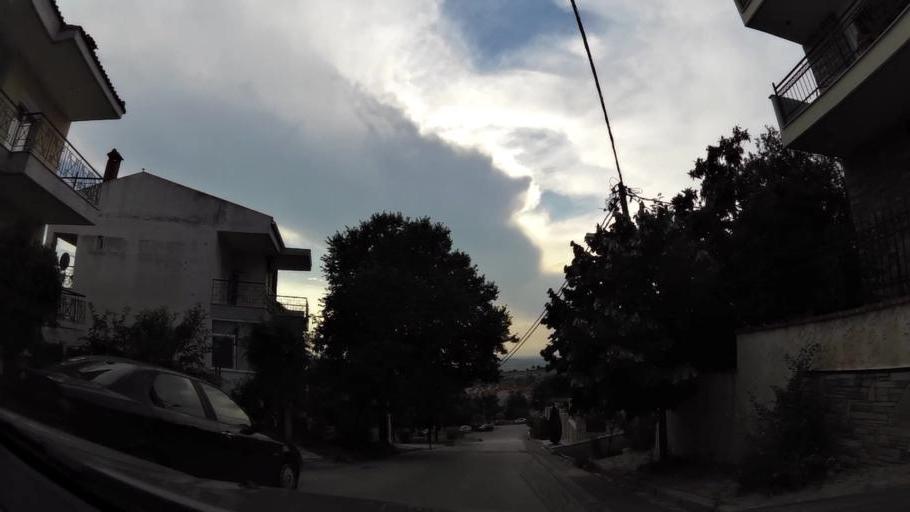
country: GR
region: Central Macedonia
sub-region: Nomos Thessalonikis
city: Pefka
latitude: 40.6628
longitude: 22.9855
